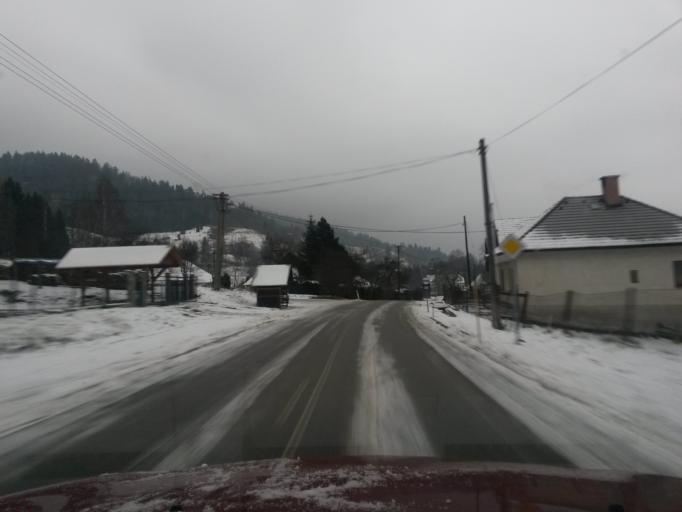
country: SK
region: Kosicky
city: Medzev
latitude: 48.7269
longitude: 20.7191
